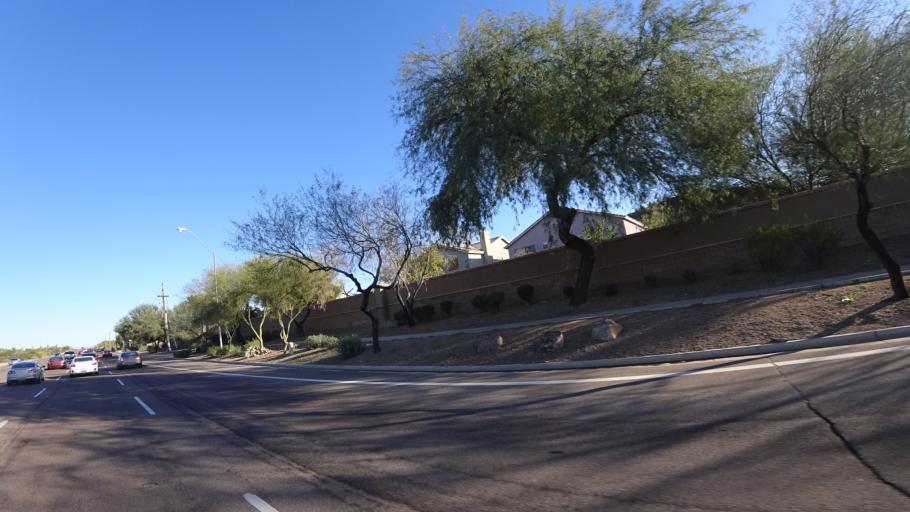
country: US
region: Arizona
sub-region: Maricopa County
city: Sun City
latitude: 33.7122
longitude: -112.1964
